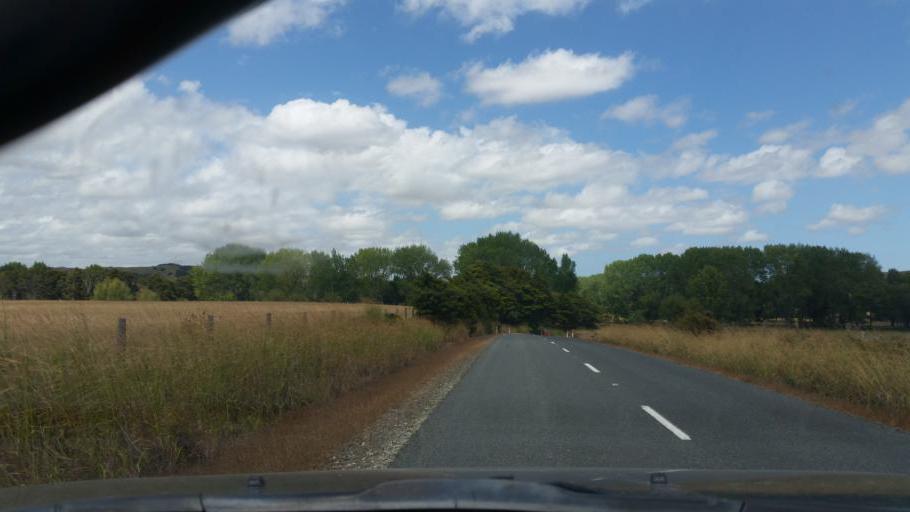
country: NZ
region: Northland
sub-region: Kaipara District
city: Dargaville
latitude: -35.8383
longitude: 173.8442
